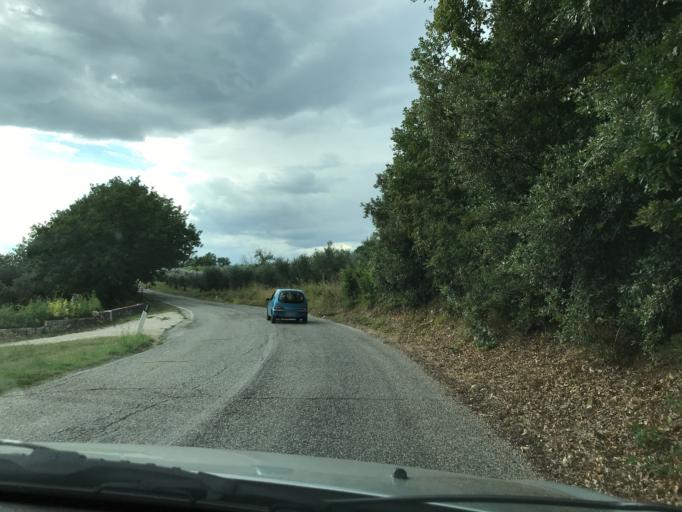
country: IT
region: Umbria
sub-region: Provincia di Terni
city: Guardea
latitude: 42.6389
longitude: 12.2914
